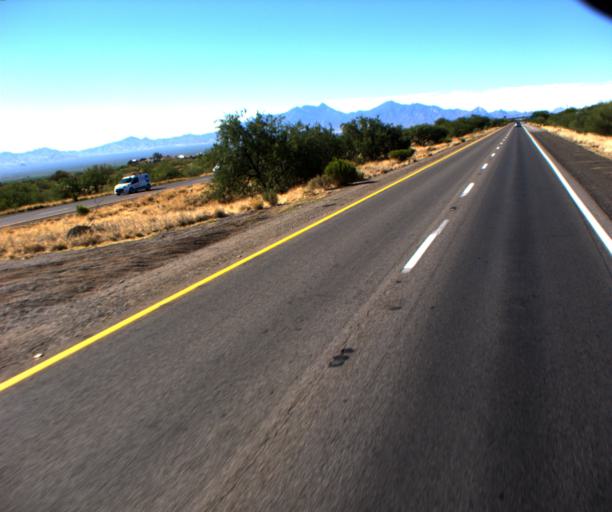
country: US
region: Arizona
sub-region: Pima County
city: Sahuarita
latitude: 31.9668
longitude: -110.9891
